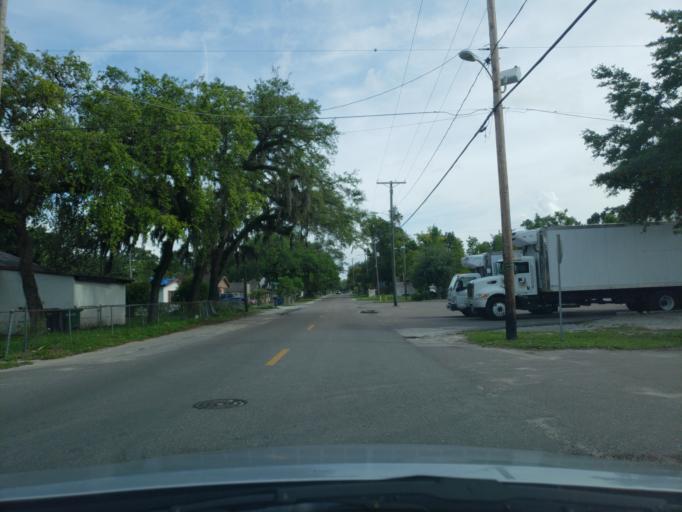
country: US
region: Florida
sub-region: Hillsborough County
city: East Lake-Orient Park
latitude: 27.9931
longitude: -82.4265
